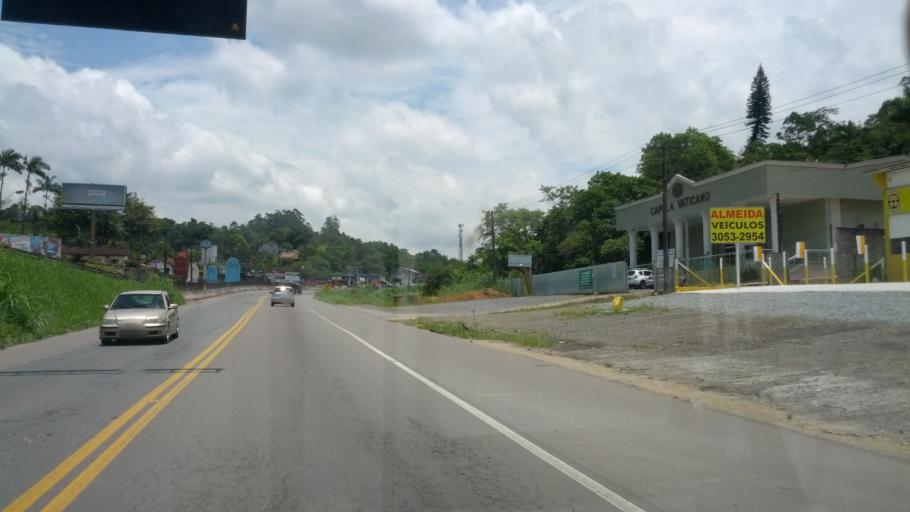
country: BR
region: Santa Catarina
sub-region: Blumenau
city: Blumenau
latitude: -26.8756
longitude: -49.1181
